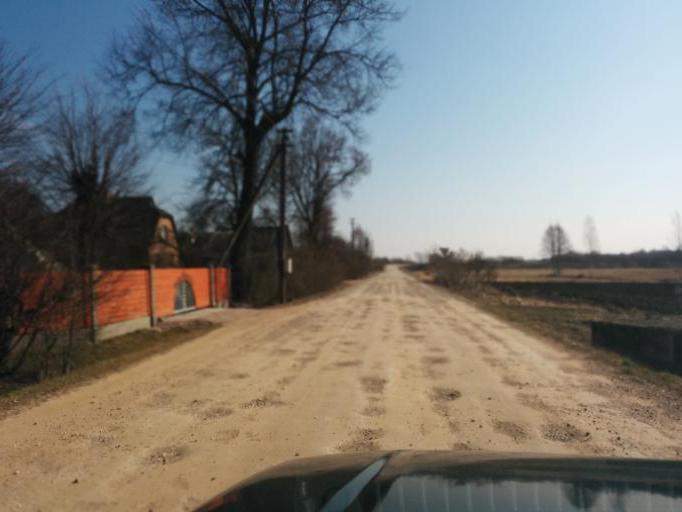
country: LV
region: Ozolnieku
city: Ozolnieki
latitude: 56.6393
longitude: 23.7863
